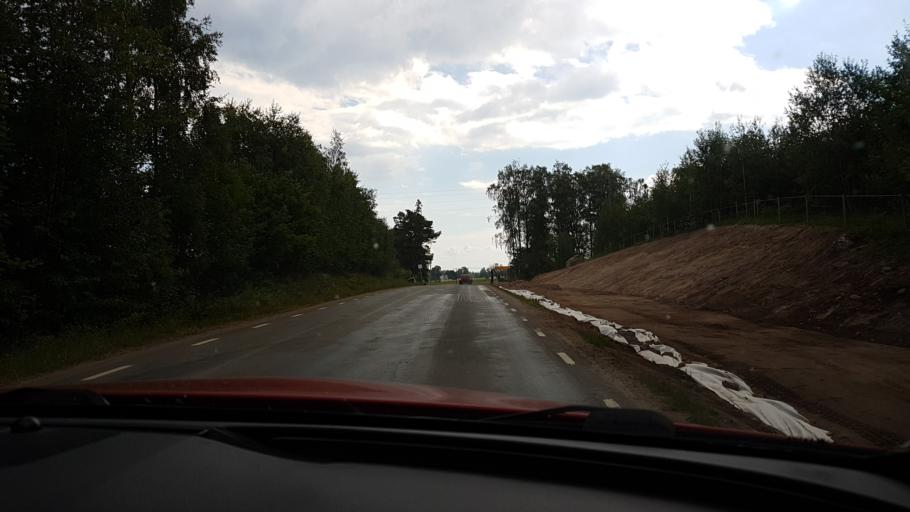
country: SE
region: Vaestra Goetaland
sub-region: Hjo Kommun
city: Hjo
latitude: 58.3084
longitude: 14.2277
